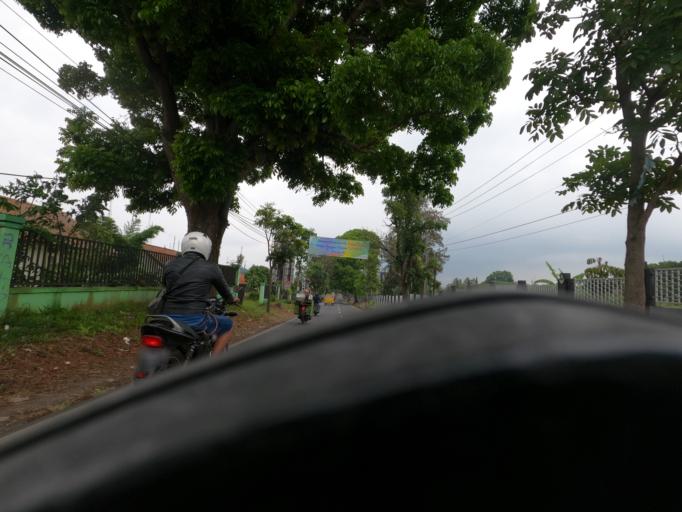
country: ID
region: West Java
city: Lembang
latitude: -6.8104
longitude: 107.5667
